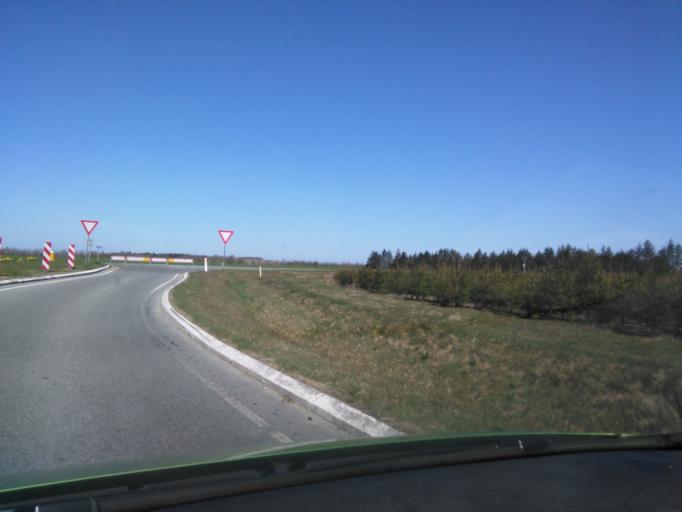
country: DK
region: South Denmark
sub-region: Billund Kommune
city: Grindsted
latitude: 55.7040
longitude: 8.8482
